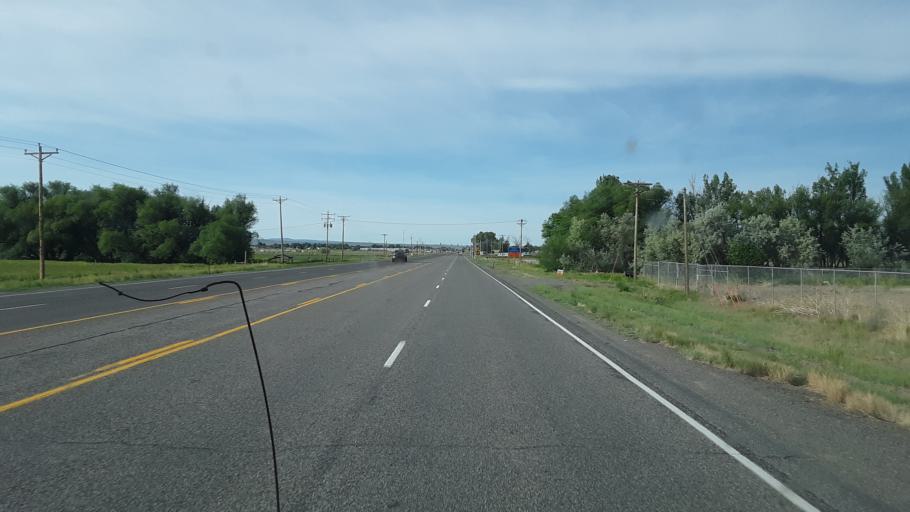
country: US
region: Wyoming
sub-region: Fremont County
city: Riverton
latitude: 43.0602
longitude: -108.3809
